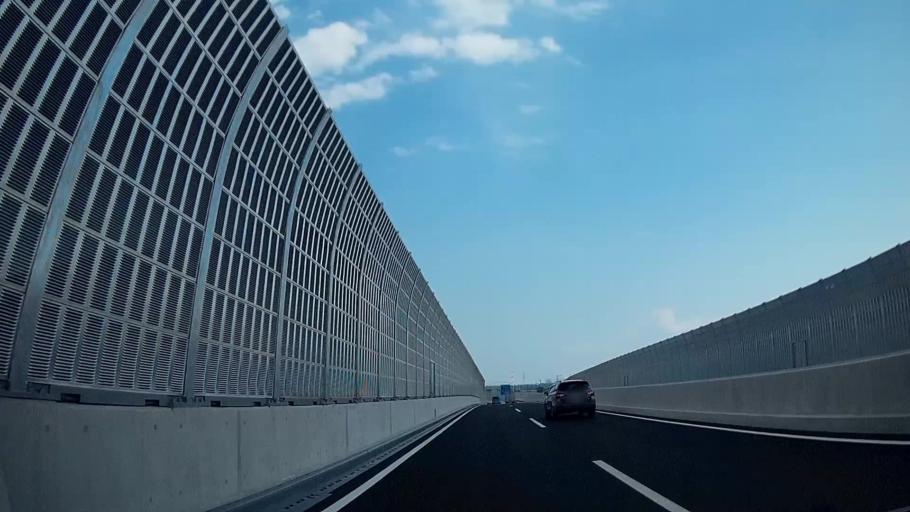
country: JP
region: Tokyo
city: Urayasu
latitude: 35.7083
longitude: 139.9254
